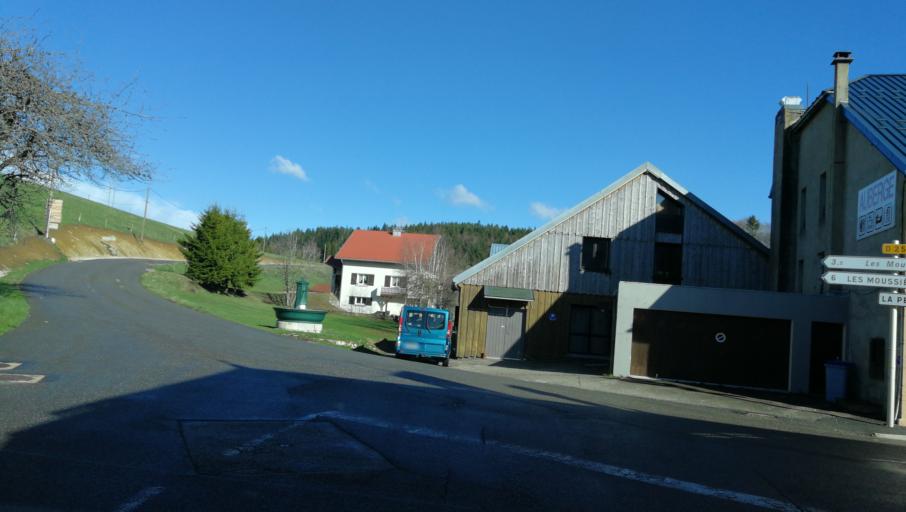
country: FR
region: Franche-Comte
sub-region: Departement du Jura
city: Saint-Claude
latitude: 46.2983
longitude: 5.8566
